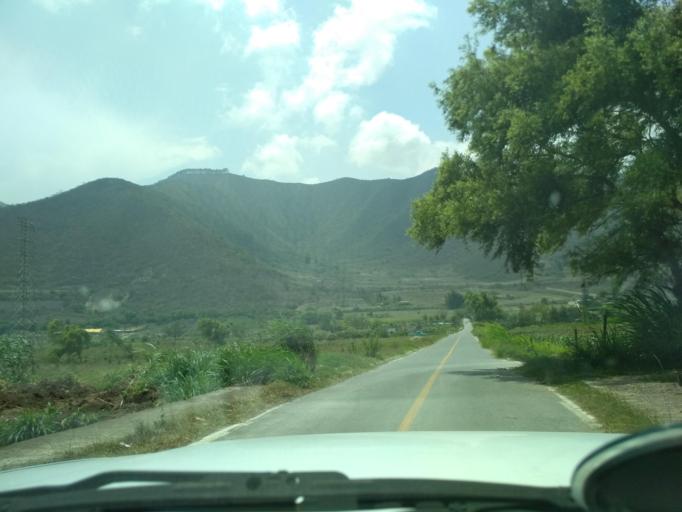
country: MX
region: Veracruz
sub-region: Nogales
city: Taza de Agua Ojo Zarco
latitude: 18.7751
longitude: -97.2179
